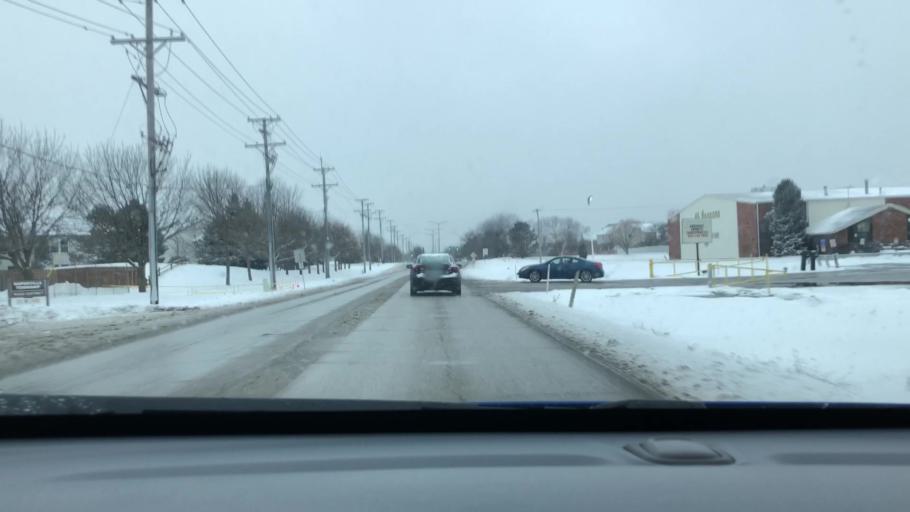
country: US
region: Illinois
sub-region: DuPage County
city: Warrenville
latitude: 41.7815
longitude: -88.2327
